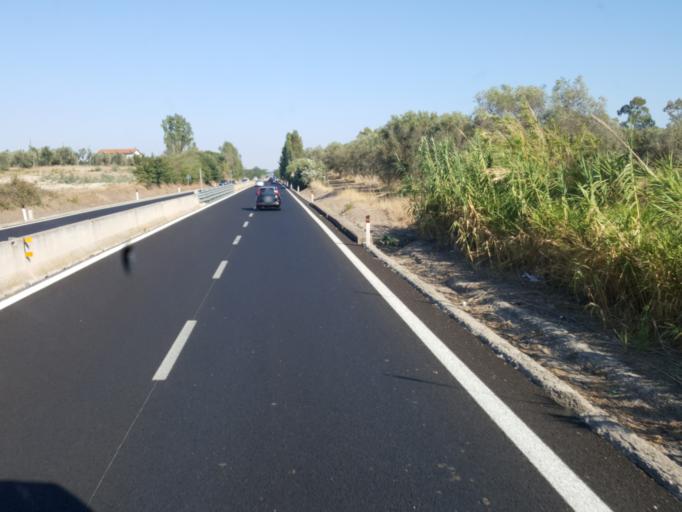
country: IT
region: Latium
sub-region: Provincia di Viterbo
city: Pescia Romana
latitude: 42.3998
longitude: 11.5083
